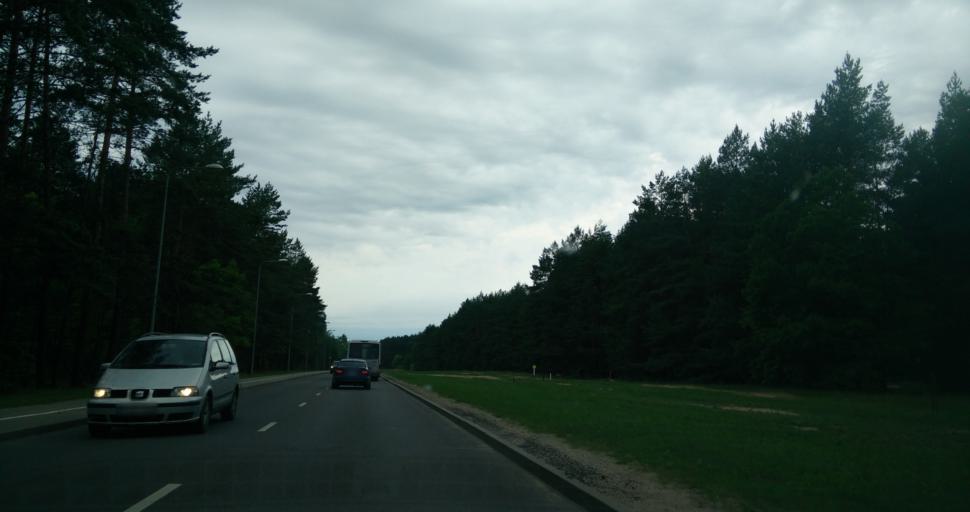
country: LT
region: Vilnius County
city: Rasos
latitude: 54.7303
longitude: 25.3549
